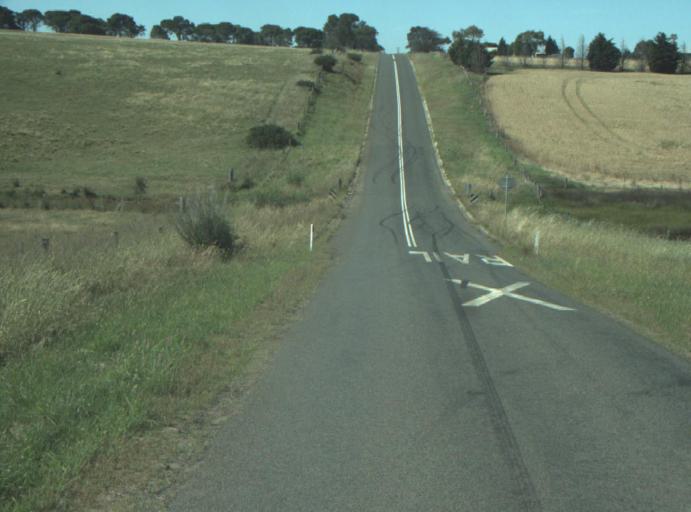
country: AU
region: Victoria
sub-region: Greater Geelong
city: Bell Post Hill
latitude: -38.0775
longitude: 144.3084
